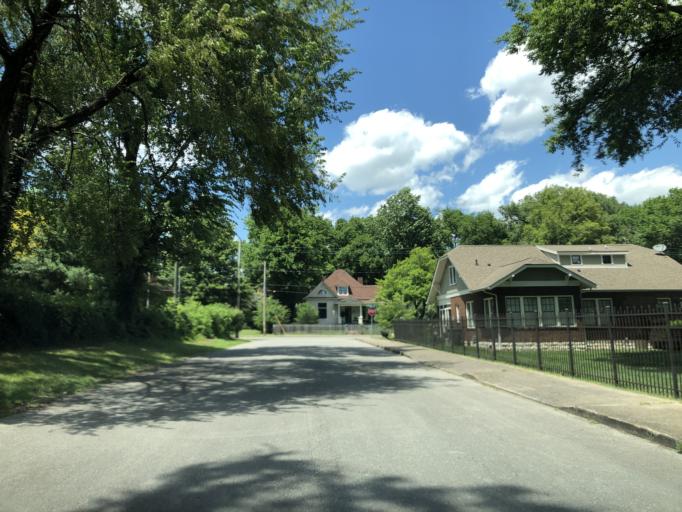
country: US
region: Tennessee
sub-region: Davidson County
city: Nashville
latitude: 36.1883
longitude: -86.7315
